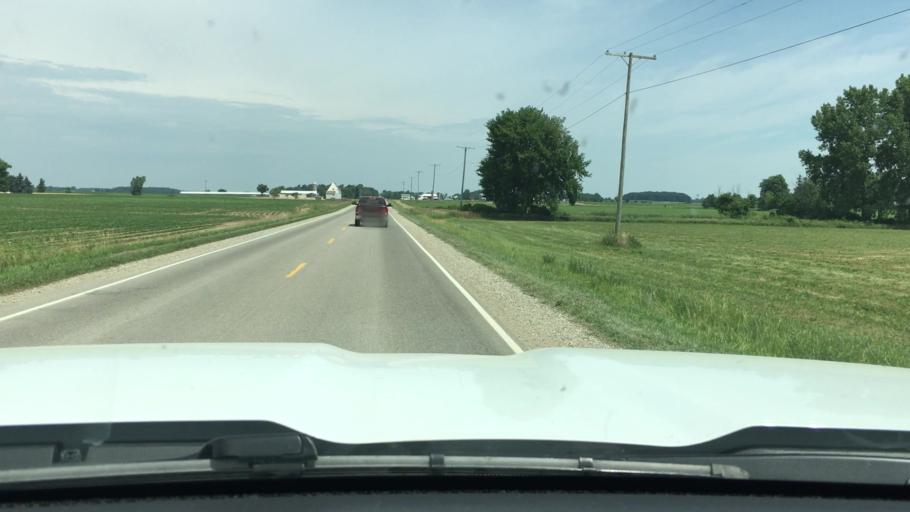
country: US
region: Michigan
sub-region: Sanilac County
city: Brown City
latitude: 43.2804
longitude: -82.9828
